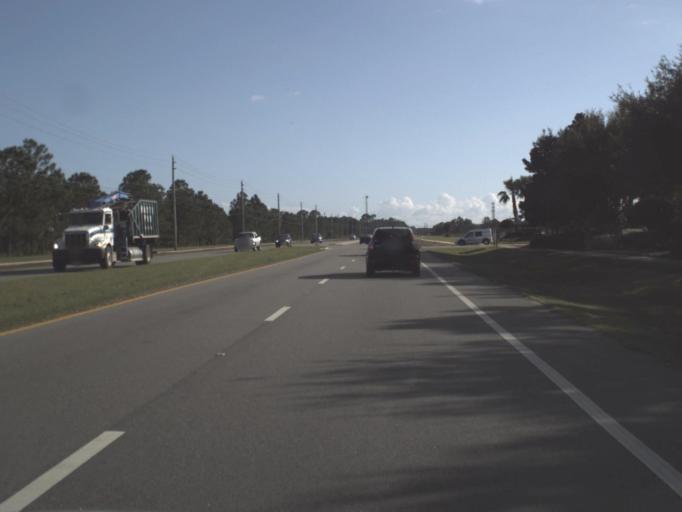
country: US
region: Florida
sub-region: Volusia County
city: Holly Hill
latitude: 29.2216
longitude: -81.0931
